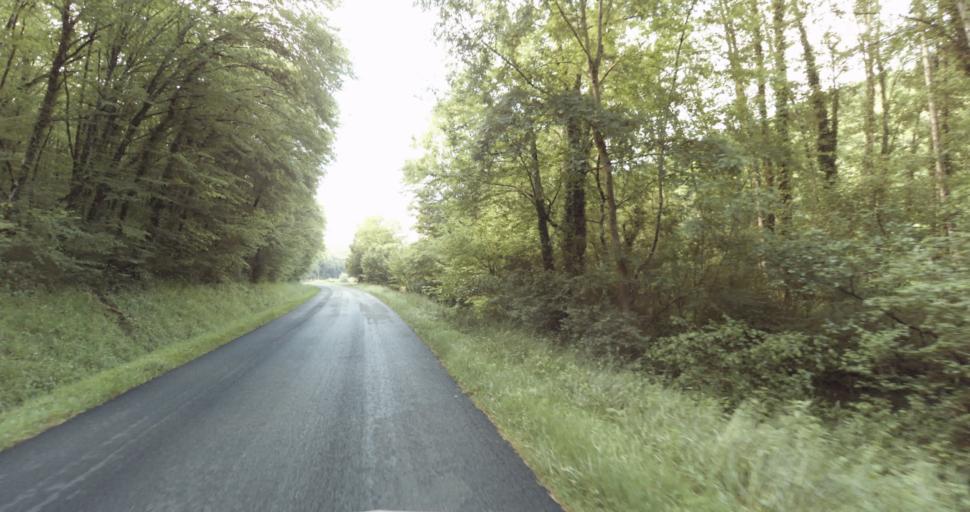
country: FR
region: Aquitaine
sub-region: Departement de la Dordogne
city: Lalinde
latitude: 44.8648
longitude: 0.7734
